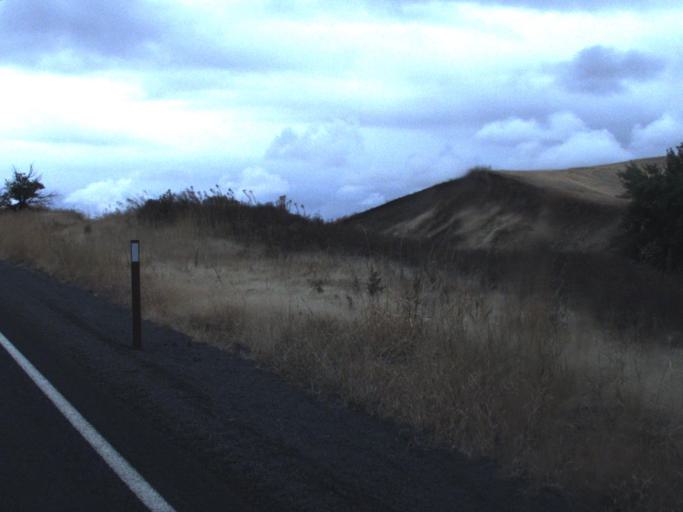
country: US
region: Washington
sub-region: Whitman County
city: Colfax
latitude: 47.1647
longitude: -117.2840
